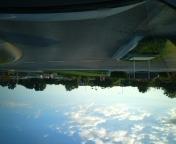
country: DE
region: Baden-Wuerttemberg
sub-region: Karlsruhe Region
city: Konigsbach-Stein
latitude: 48.9541
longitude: 8.5847
